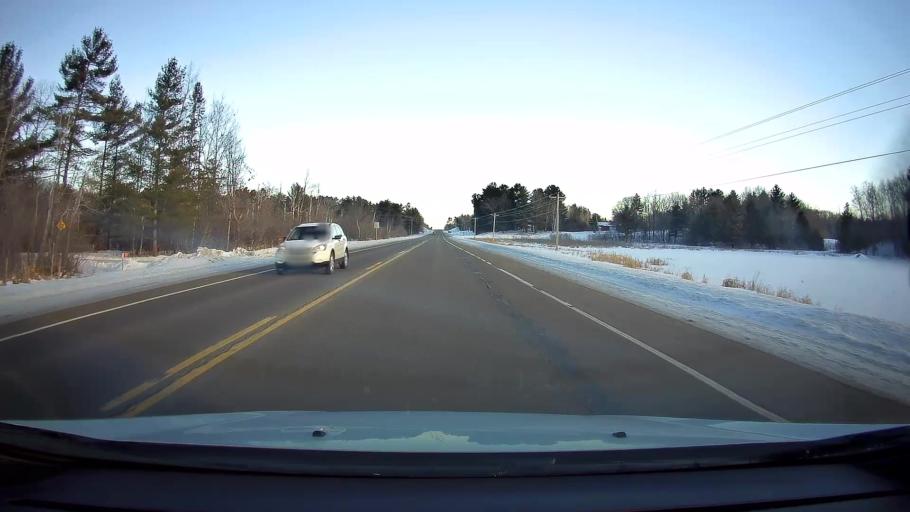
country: US
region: Wisconsin
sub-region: Barron County
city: Cumberland
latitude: 45.5771
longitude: -92.0175
